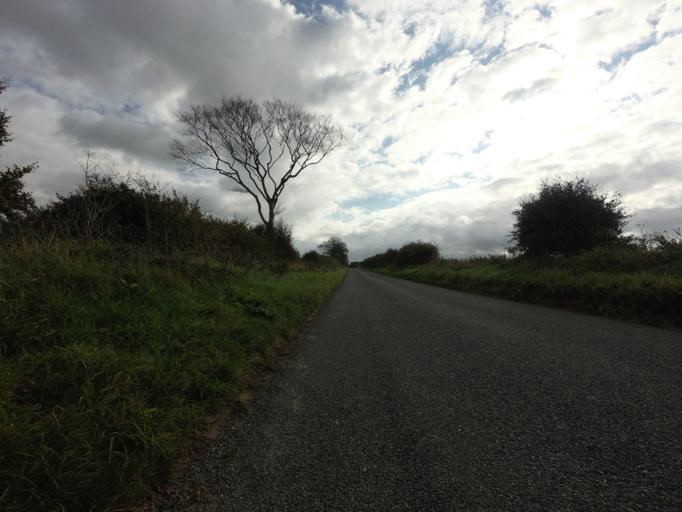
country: GB
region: England
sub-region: Norfolk
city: Heacham
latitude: 52.9217
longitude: 0.5410
